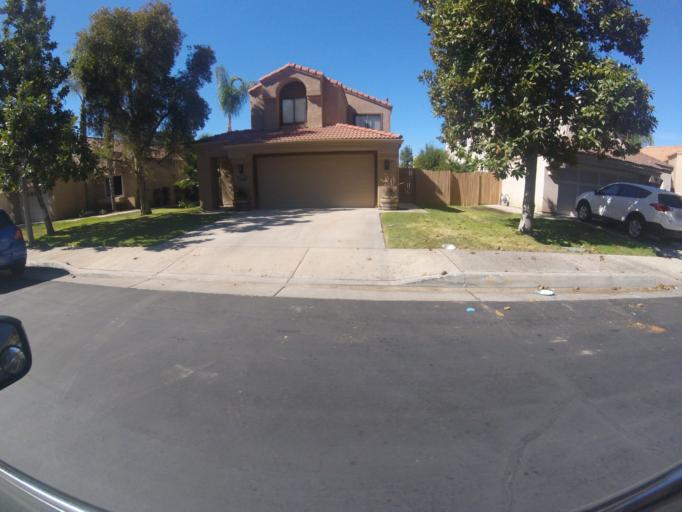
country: US
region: California
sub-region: San Bernardino County
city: Mentone
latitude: 34.0673
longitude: -117.1428
